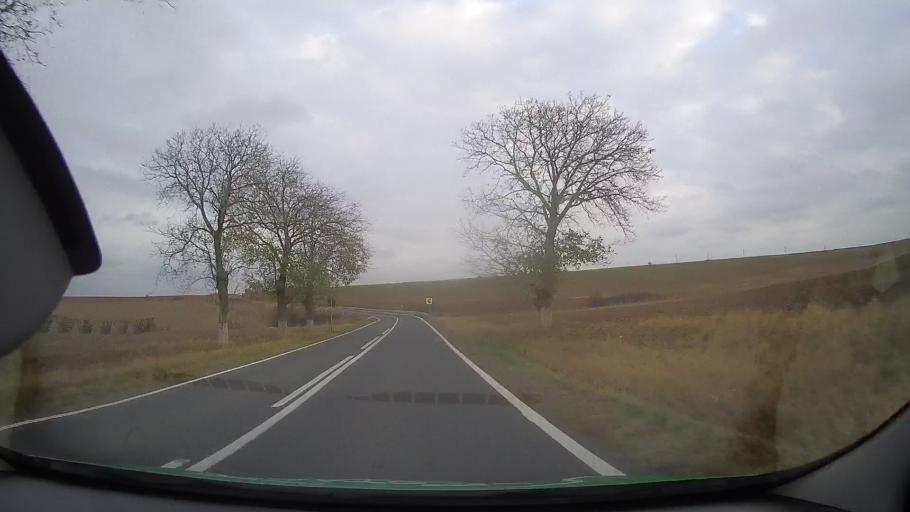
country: RO
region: Constanta
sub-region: Comuna Adamclisi
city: Adamclisi
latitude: 44.0877
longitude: 27.9762
